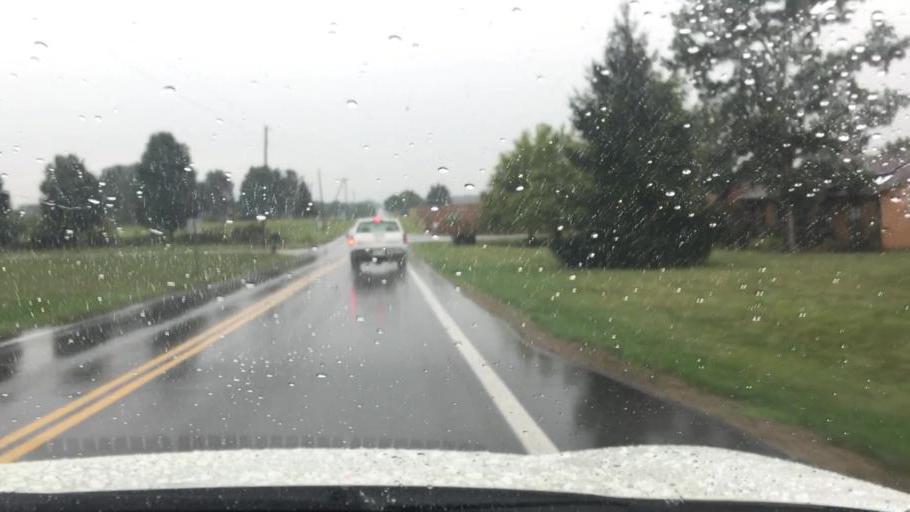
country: US
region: Ohio
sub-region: Champaign County
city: Urbana
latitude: 40.0966
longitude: -83.7327
